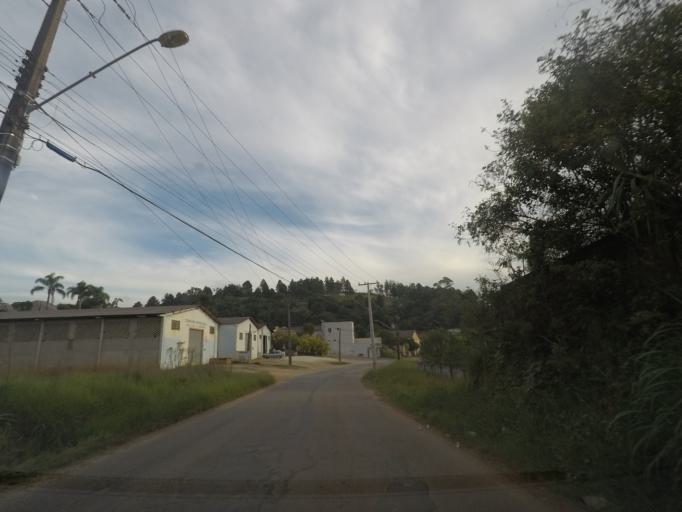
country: BR
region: Parana
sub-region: Colombo
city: Colombo
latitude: -25.2877
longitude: -49.2146
